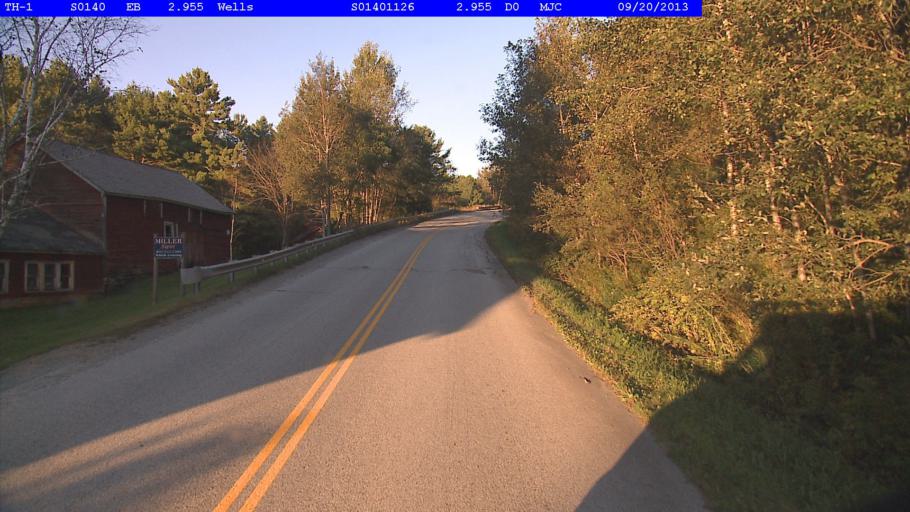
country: US
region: New York
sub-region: Washington County
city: Granville
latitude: 43.4105
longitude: -73.1497
